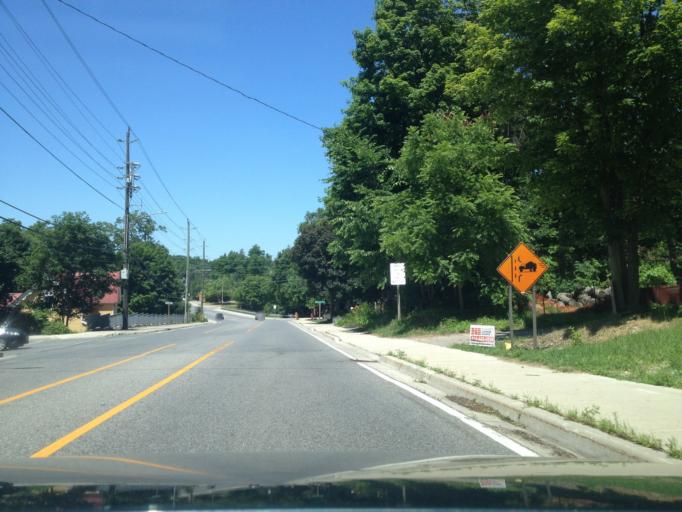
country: CA
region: Ontario
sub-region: Wellington County
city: Guelph
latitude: 43.6128
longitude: -80.1355
